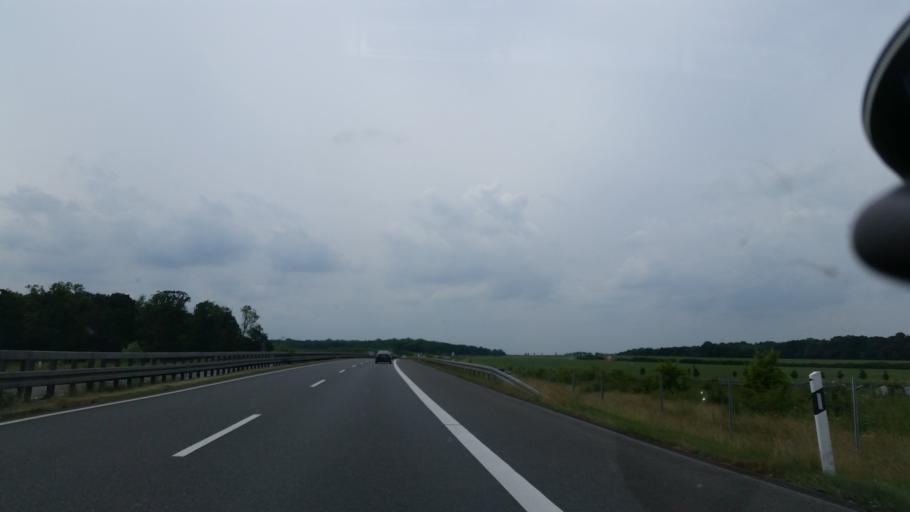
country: DE
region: Lower Saxony
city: Cremlingen
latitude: 52.2629
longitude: 10.6881
